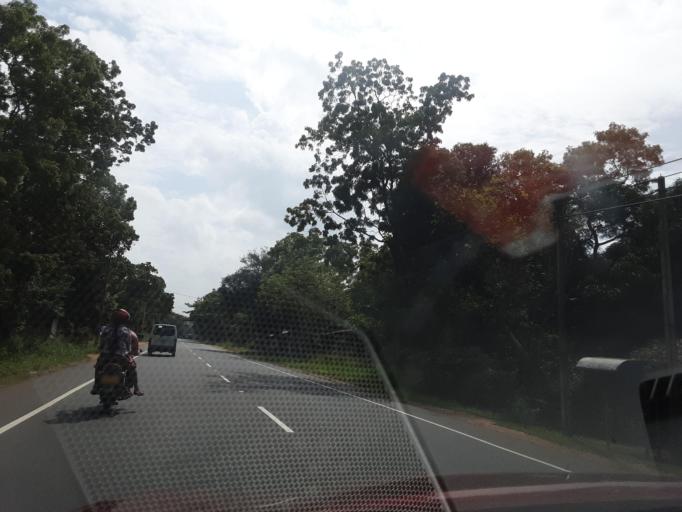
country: LK
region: North Central
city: Anuradhapura
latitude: 8.4965
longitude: 80.5121
